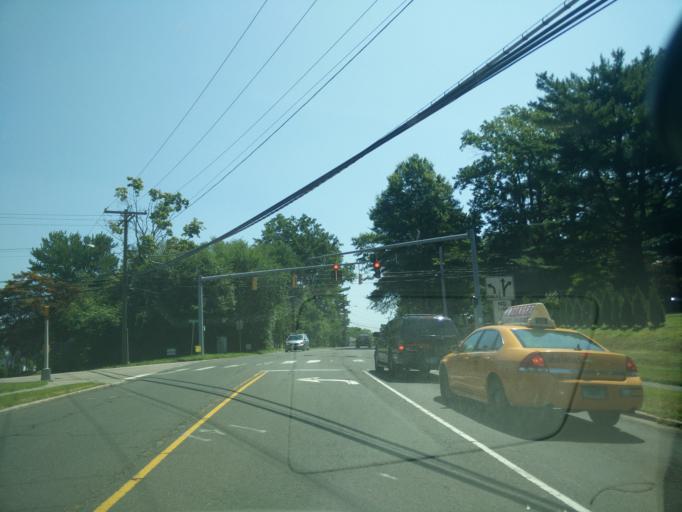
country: US
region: Connecticut
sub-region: Fairfield County
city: Bridgeport
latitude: 41.1784
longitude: -73.2366
